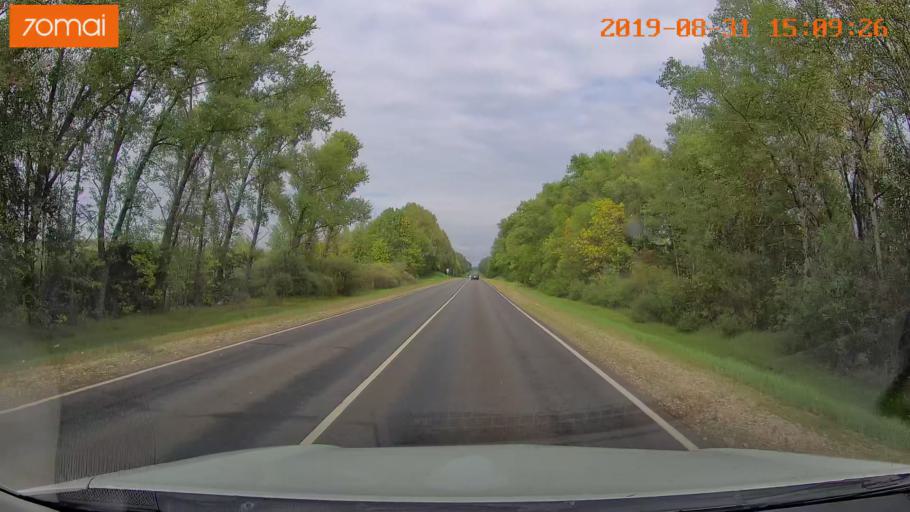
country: RU
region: Kaluga
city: Spas-Demensk
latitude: 54.4019
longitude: 34.2008
